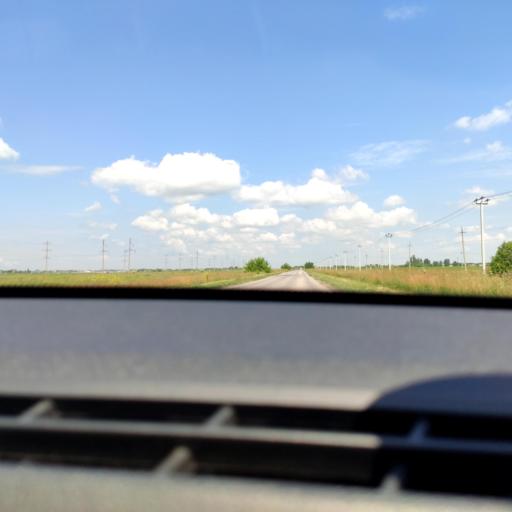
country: RU
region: Samara
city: Podstepki
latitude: 53.5496
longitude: 49.0895
